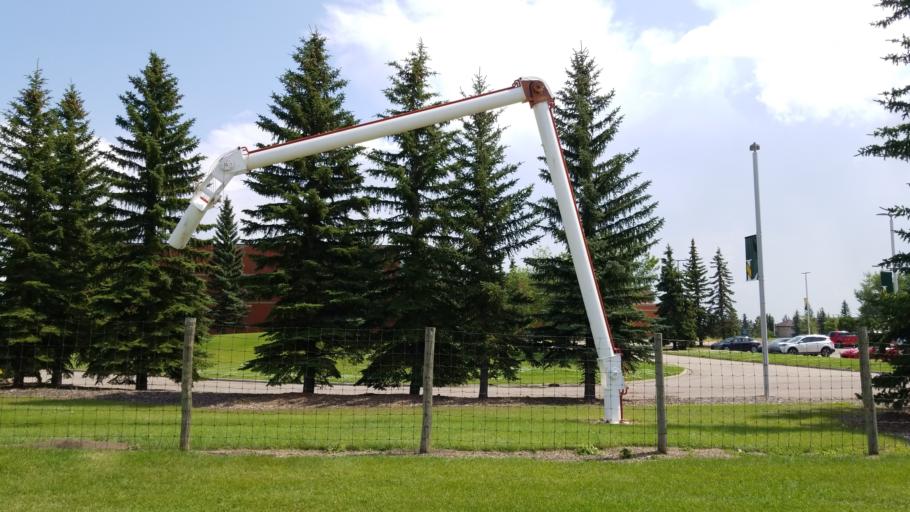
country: CA
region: Saskatchewan
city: Lloydminster
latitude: 53.2618
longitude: -110.0357
